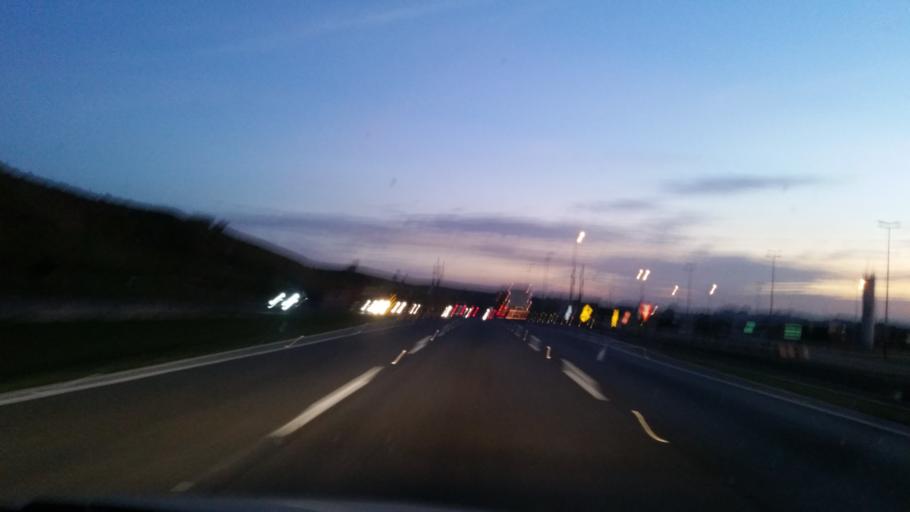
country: BR
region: Sao Paulo
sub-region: Santa Isabel
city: Santa Isabel
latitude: -23.3773
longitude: -46.1438
